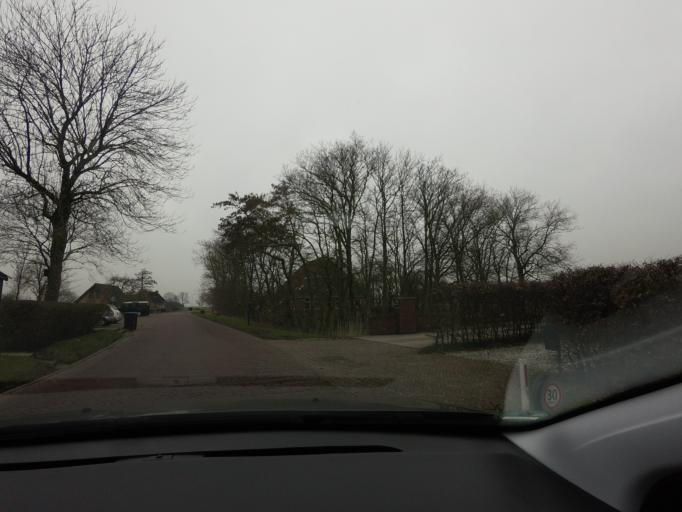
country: NL
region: Friesland
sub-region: Sudwest Fryslan
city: Bolsward
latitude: 53.1099
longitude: 5.5384
